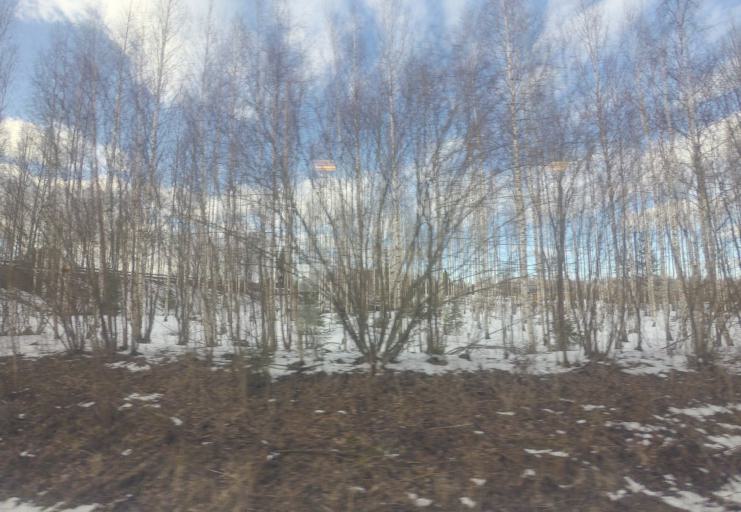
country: FI
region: Southern Savonia
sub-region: Savonlinna
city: Kerimaeki
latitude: 61.8341
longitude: 29.1981
